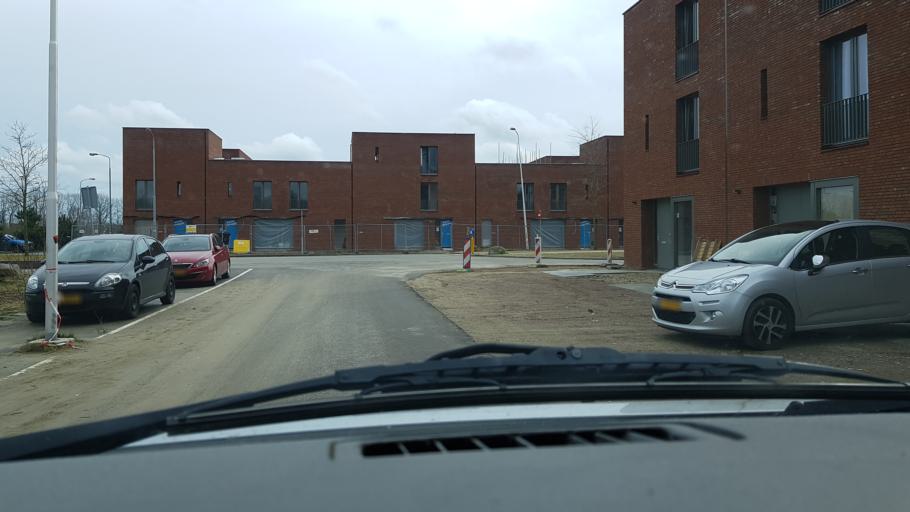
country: NL
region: North Brabant
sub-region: Gemeente Eindhoven
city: Meerhoven
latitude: 51.4395
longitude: 5.4021
